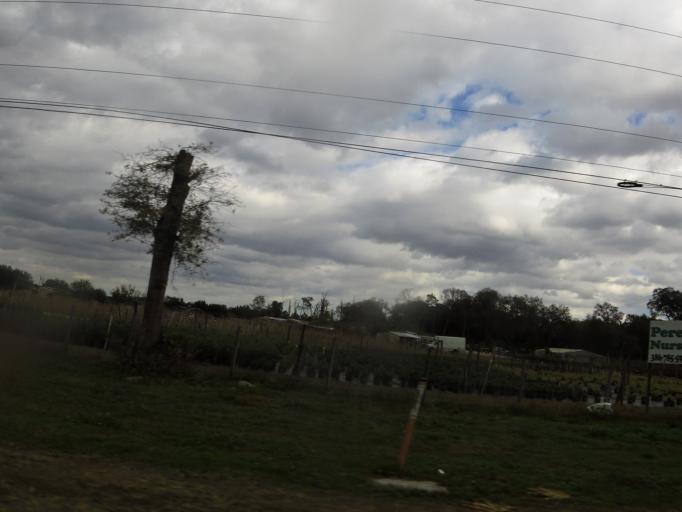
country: US
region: Florida
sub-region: Volusia County
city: Pierson
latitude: 29.3094
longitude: -81.4896
